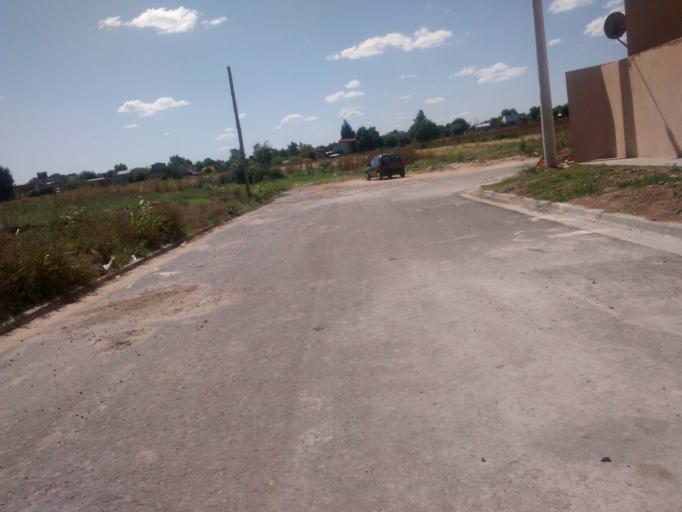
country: AR
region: Buenos Aires
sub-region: Partido de La Plata
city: La Plata
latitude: -34.9353
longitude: -57.9089
